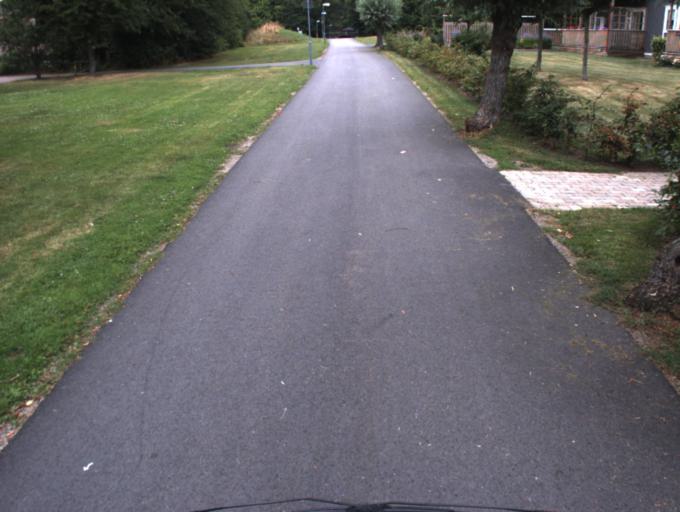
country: SE
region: Skane
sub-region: Helsingborg
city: Helsingborg
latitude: 56.0602
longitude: 12.7259
